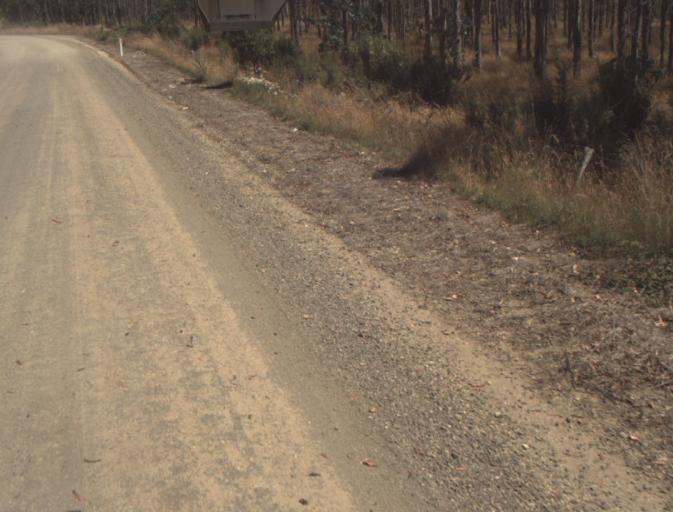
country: AU
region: Tasmania
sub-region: Dorset
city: Scottsdale
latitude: -41.3244
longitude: 147.4452
